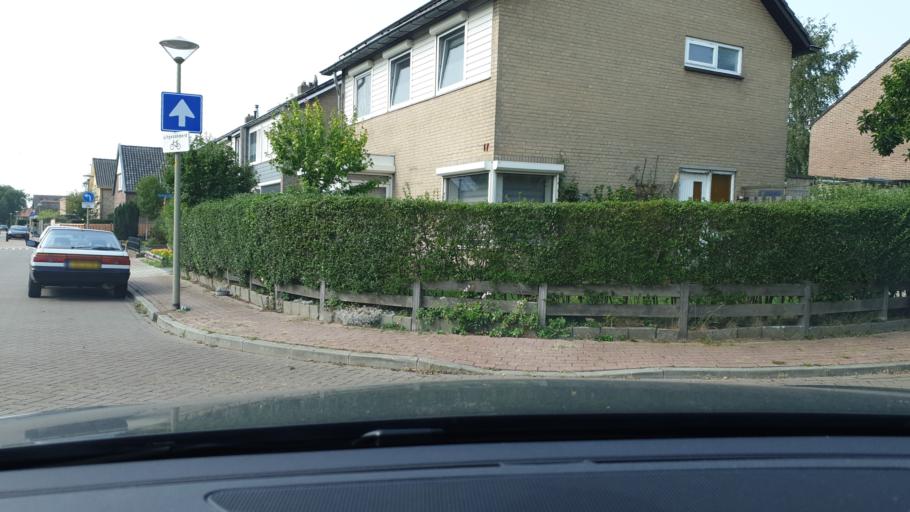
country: NL
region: Gelderland
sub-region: Gemeente Zevenaar
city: Zevenaar
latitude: 51.8613
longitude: 6.0575
